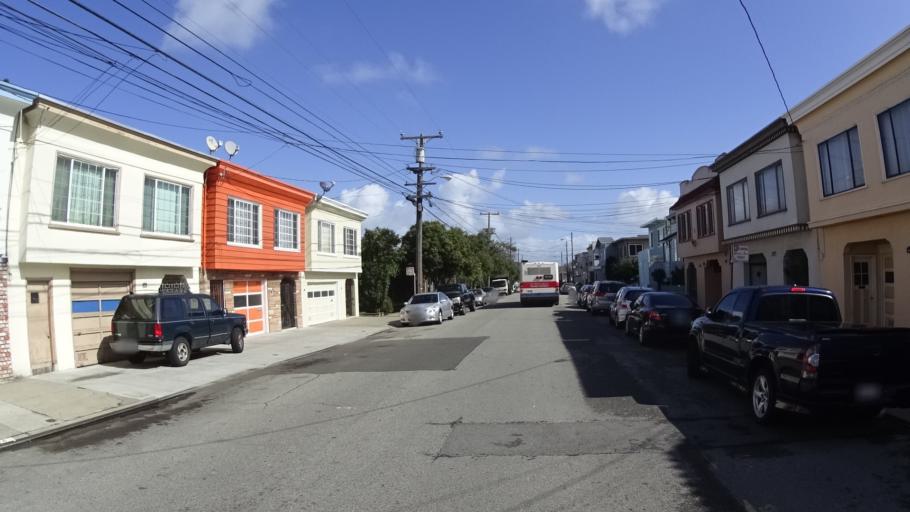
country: US
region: California
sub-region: San Mateo County
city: Daly City
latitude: 37.7092
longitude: -122.4474
